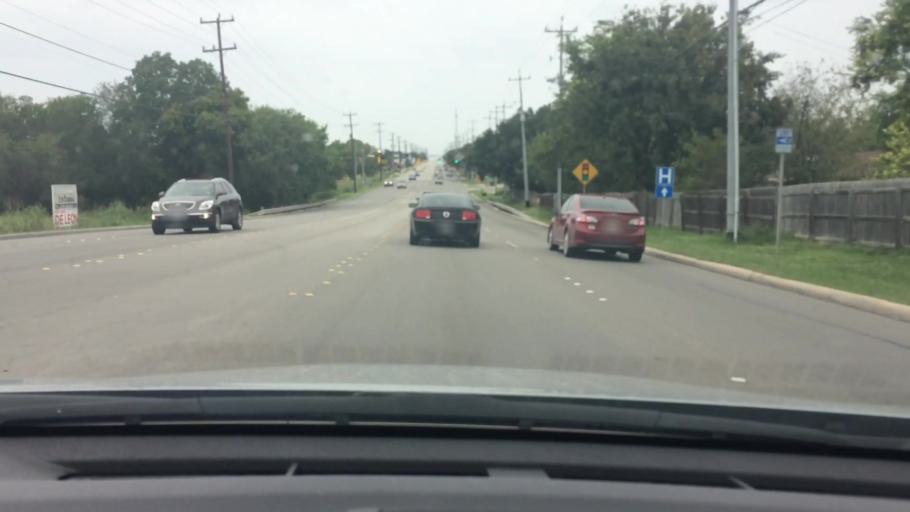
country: US
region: Texas
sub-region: Bexar County
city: Live Oak
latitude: 29.5387
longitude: -98.3371
